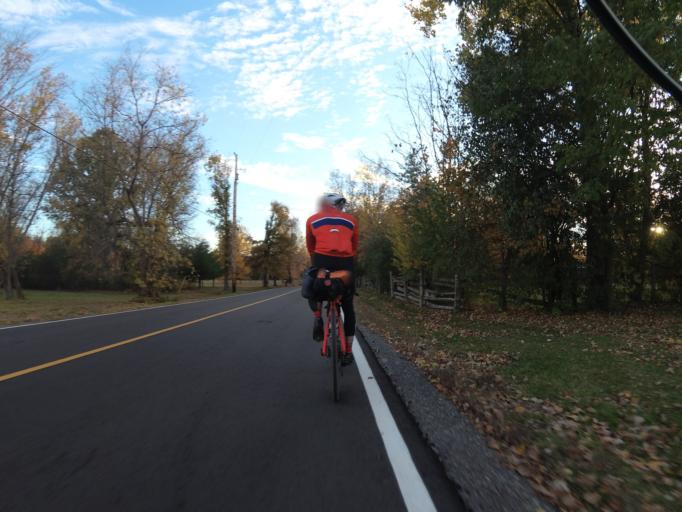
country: CA
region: Ontario
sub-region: Lanark County
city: Smiths Falls
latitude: 44.9440
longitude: -75.8214
